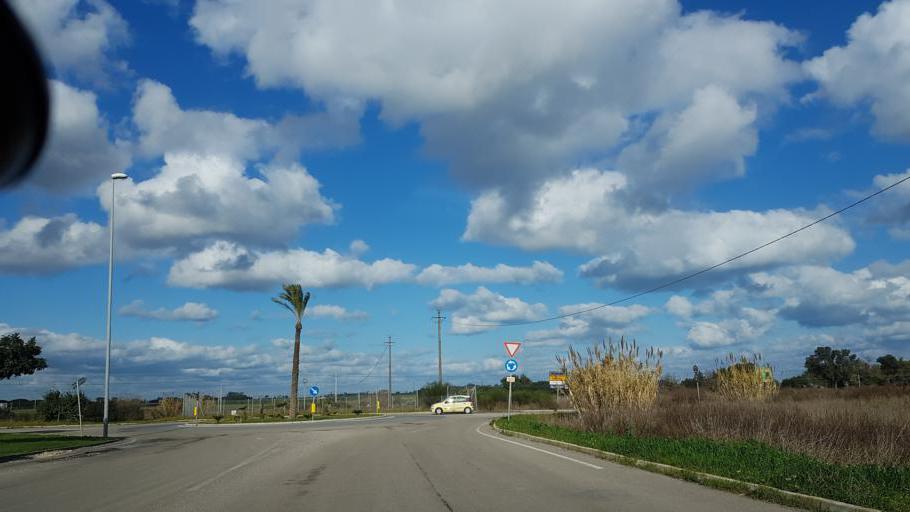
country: IT
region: Apulia
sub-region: Provincia di Brindisi
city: Brindisi
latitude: 40.6206
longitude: 17.9038
